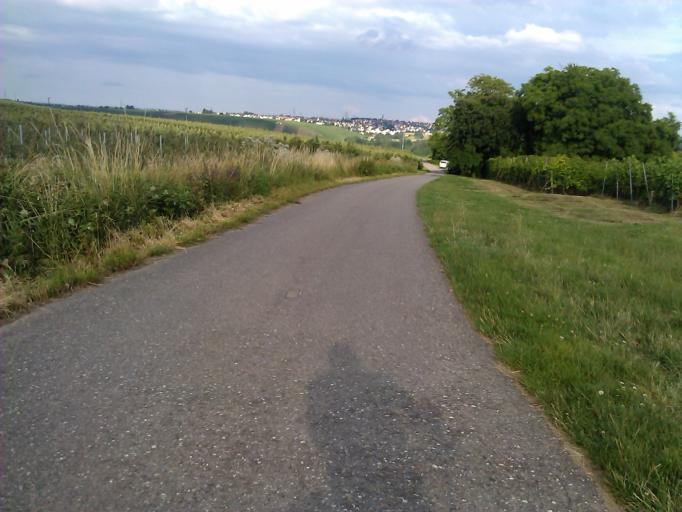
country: DE
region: Baden-Wuerttemberg
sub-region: Regierungsbezirk Stuttgart
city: Kirchheim am Neckar
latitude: 49.0513
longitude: 9.1552
